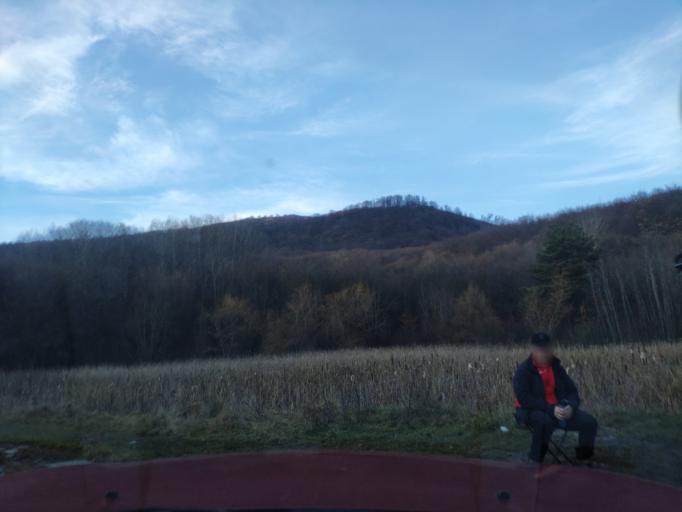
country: SK
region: Kosicky
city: Secovce
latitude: 48.6360
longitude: 21.4650
